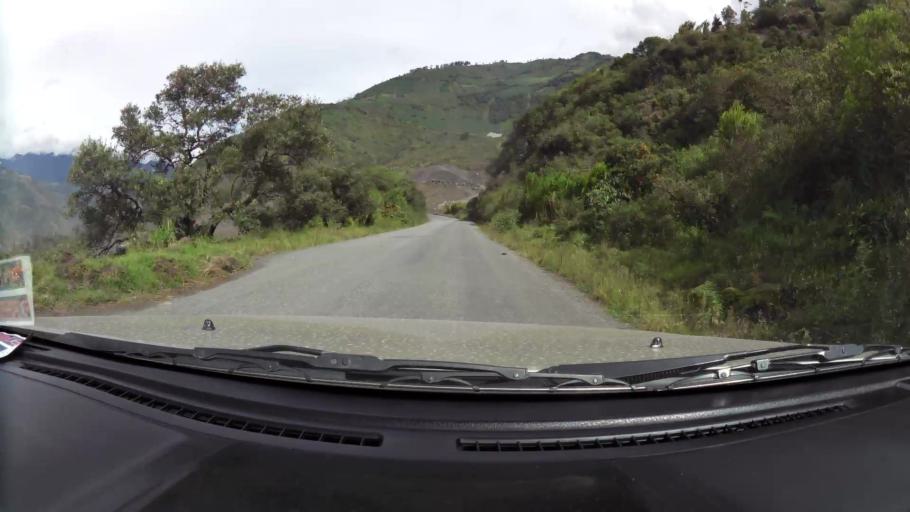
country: EC
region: Tungurahua
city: Banos
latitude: -1.4121
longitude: -78.4708
